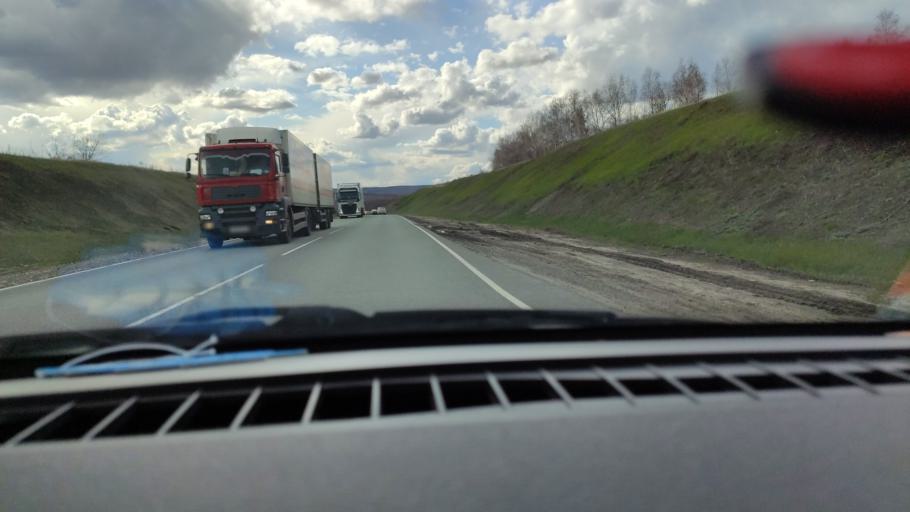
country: RU
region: Saratov
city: Tersa
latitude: 52.1035
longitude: 47.4921
